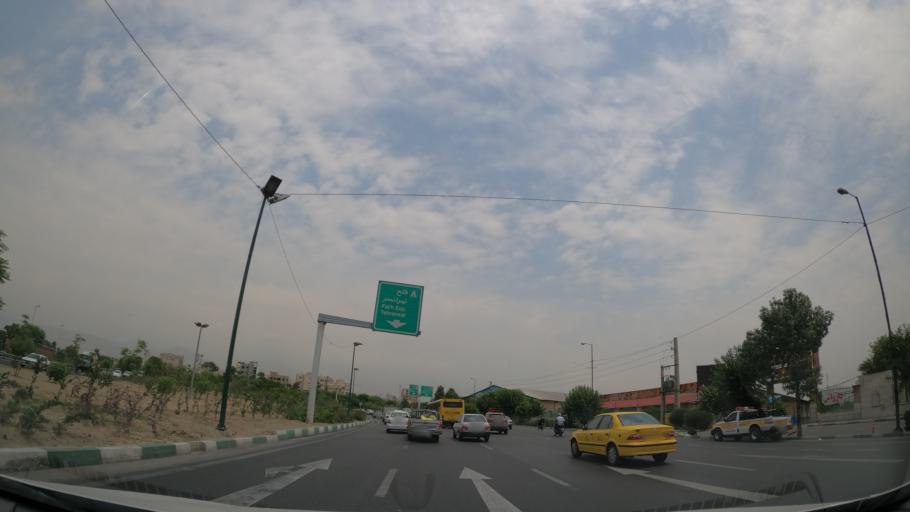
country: IR
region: Tehran
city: Tehran
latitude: 35.6820
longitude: 51.3429
